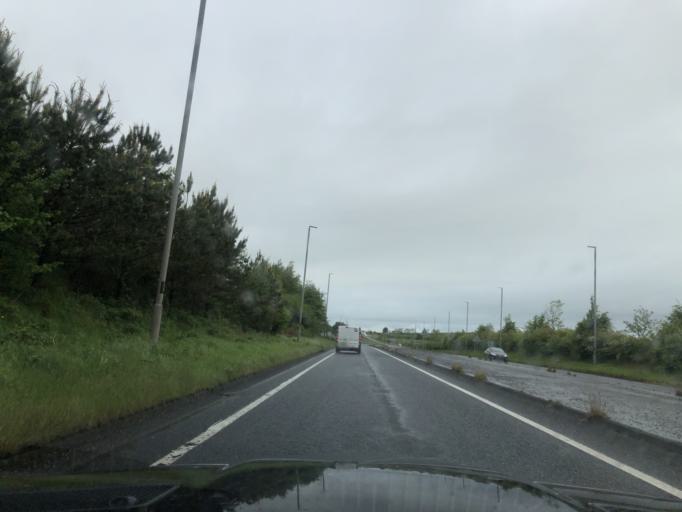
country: GB
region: Northern Ireland
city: Dunloy
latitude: 55.0222
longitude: -6.3817
